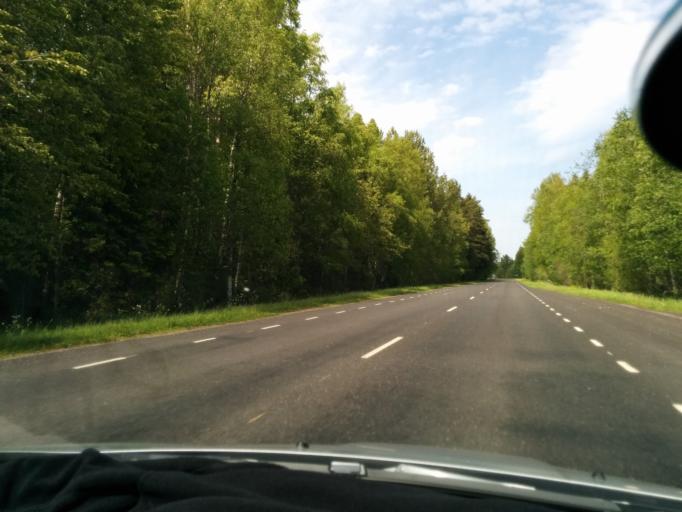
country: EE
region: Harju
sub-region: Loksa linn
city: Loksa
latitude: 59.5620
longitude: 25.7249
